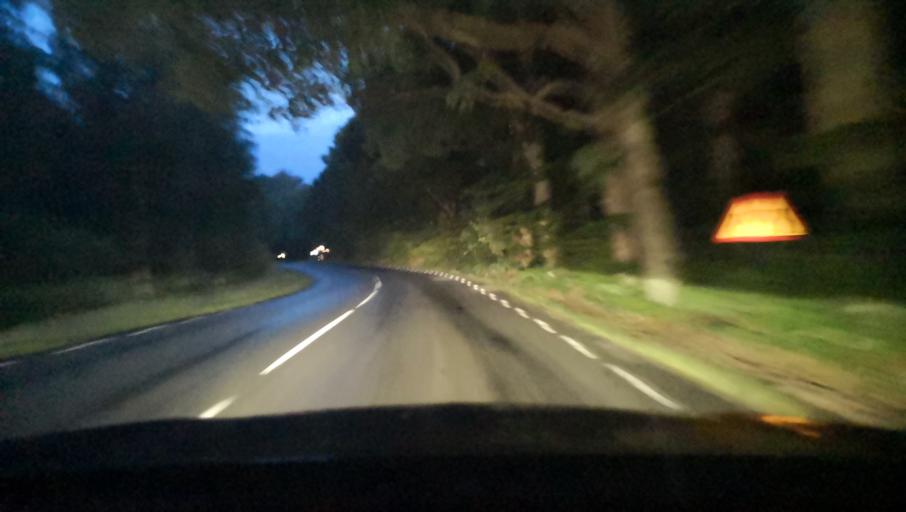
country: SE
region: Skane
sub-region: Osby Kommun
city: Osby
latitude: 56.3522
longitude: 13.9718
